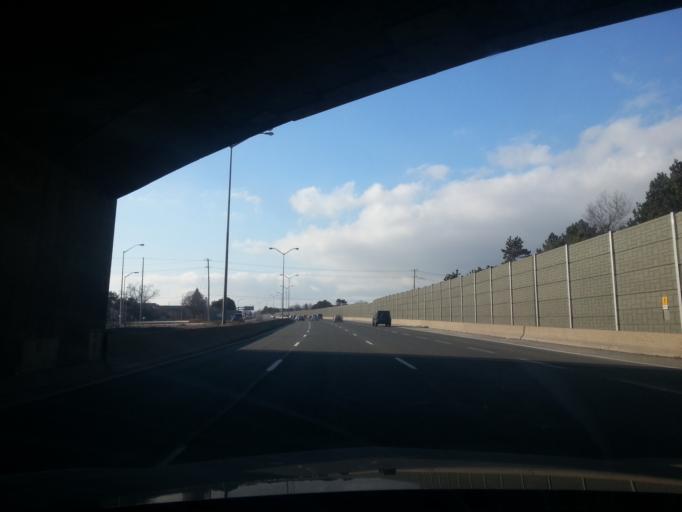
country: CA
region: Ontario
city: Oshawa
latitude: 43.8871
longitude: -78.8290
